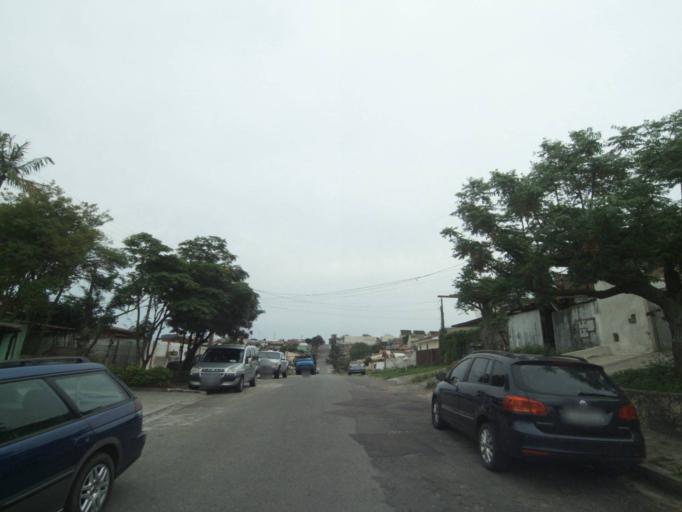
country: BR
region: Parana
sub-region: Pinhais
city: Pinhais
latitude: -25.4078
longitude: -49.1994
